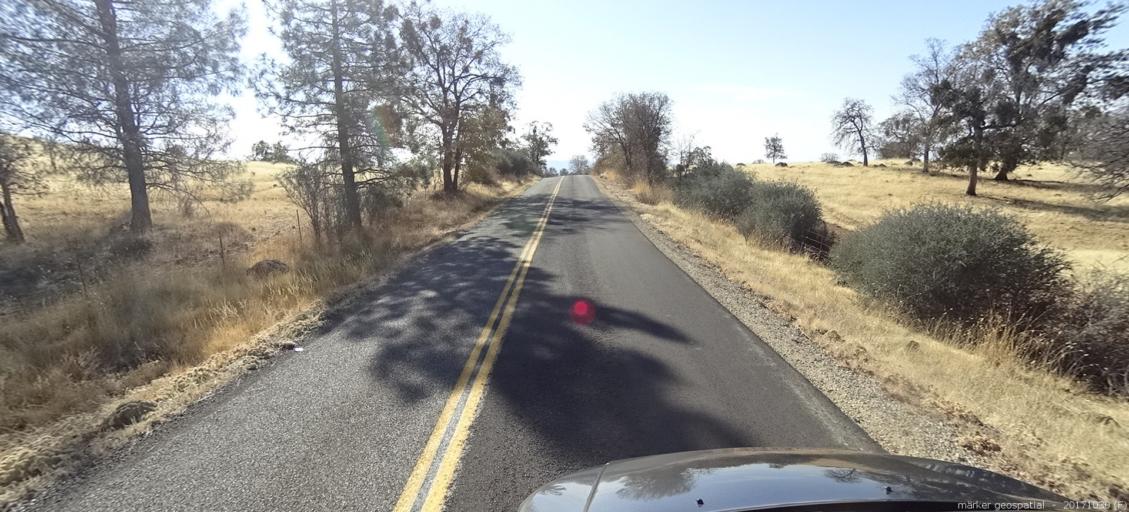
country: US
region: California
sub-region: Shasta County
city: Shingletown
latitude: 40.6747
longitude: -121.9467
